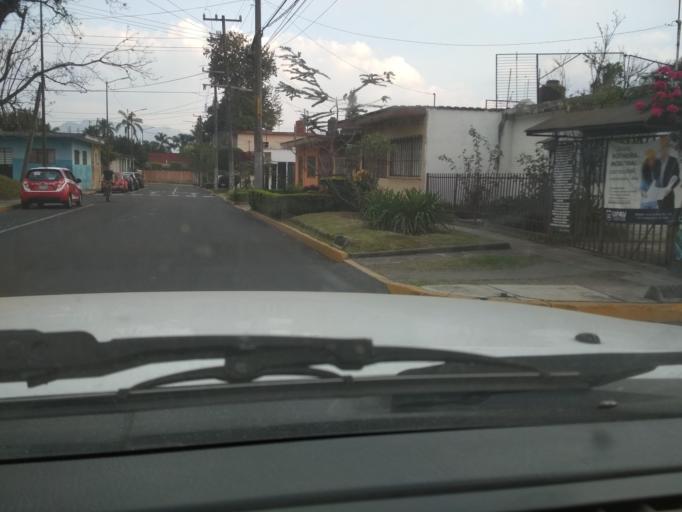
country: MX
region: Veracruz
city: Orizaba
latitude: 18.8658
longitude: -97.0999
